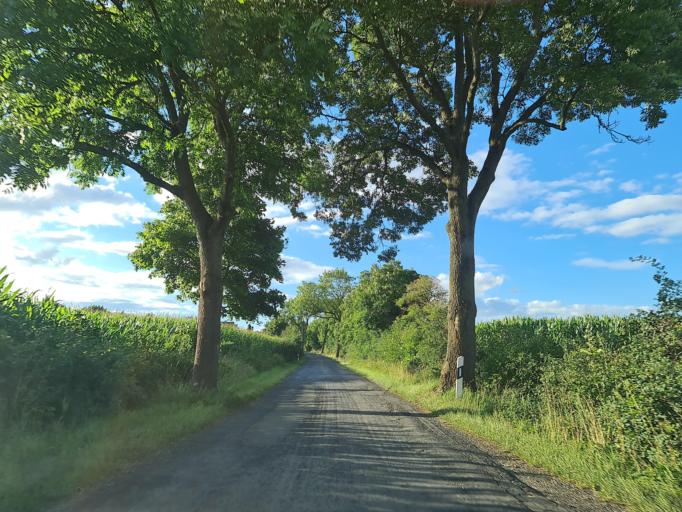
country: DE
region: Saxony
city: Syrau
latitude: 50.5353
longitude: 12.0825
